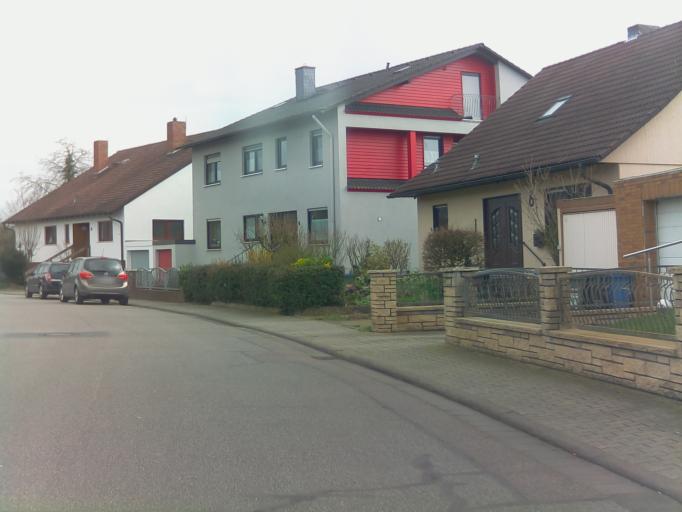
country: DE
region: Hesse
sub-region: Regierungsbezirk Darmstadt
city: Alsbach-Hahnlein
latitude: 49.7328
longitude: 8.5701
